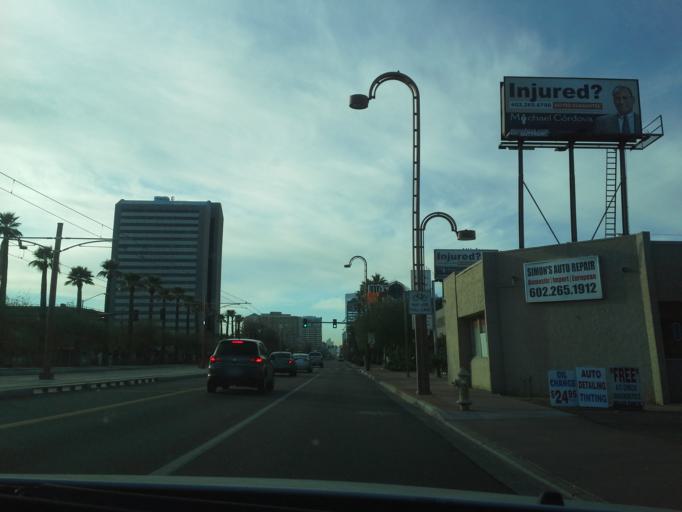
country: US
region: Arizona
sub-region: Maricopa County
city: Phoenix
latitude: 33.4974
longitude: -112.0739
